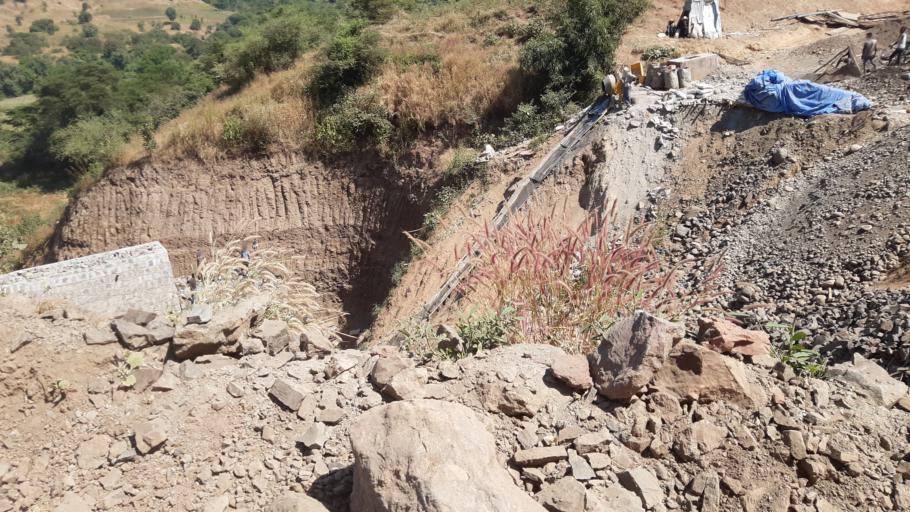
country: ET
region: Amhara
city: Dabat
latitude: 13.1923
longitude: 37.5633
